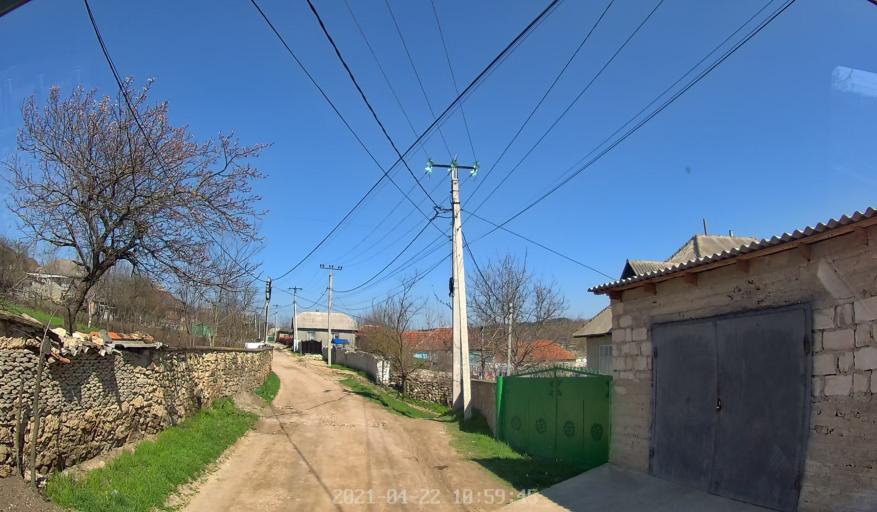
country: MD
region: Chisinau
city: Ciorescu
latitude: 47.1708
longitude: 28.9495
